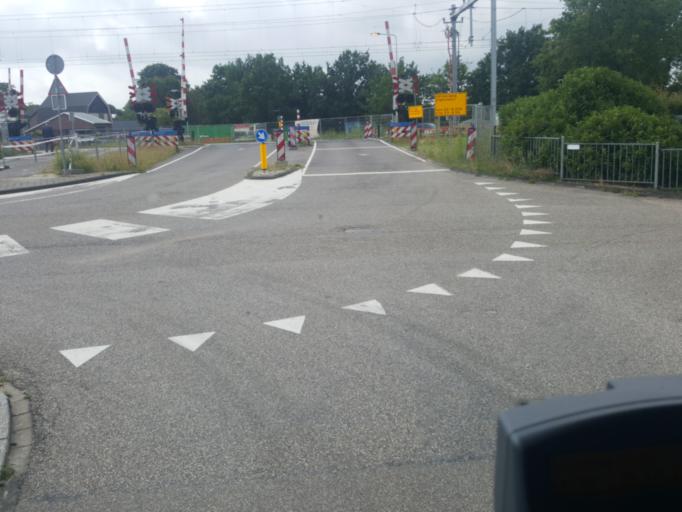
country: NL
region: Utrecht
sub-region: Gemeente Utrechtse Heuvelrug
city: Driebergen-Rijsenburg
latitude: 52.0657
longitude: 5.2557
